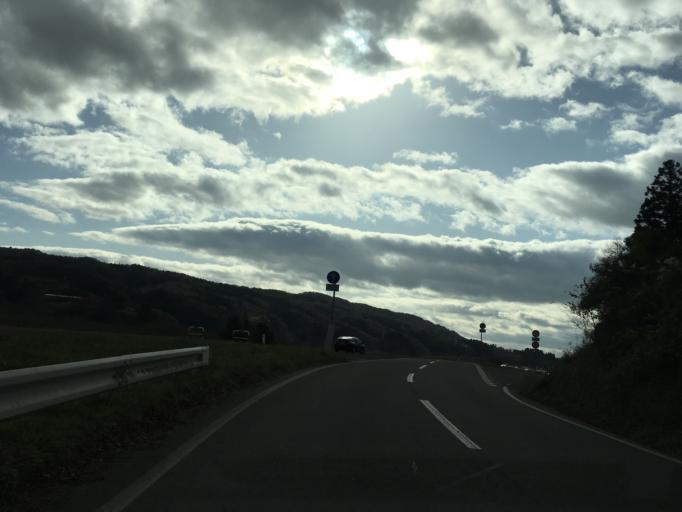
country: JP
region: Iwate
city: Ichinoseki
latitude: 38.8402
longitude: 141.2591
